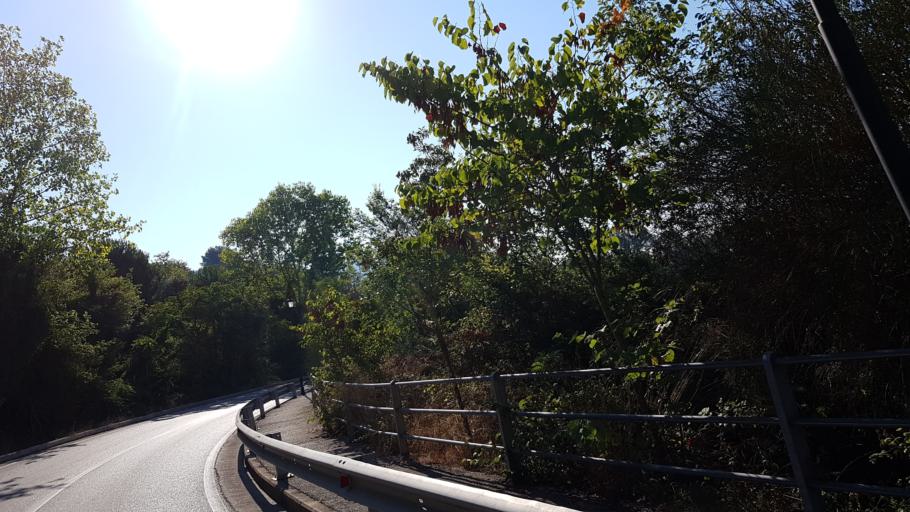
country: AL
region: Vlore
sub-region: Rrethi i Sarandes
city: Xarre
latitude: 39.7459
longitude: 20.0166
